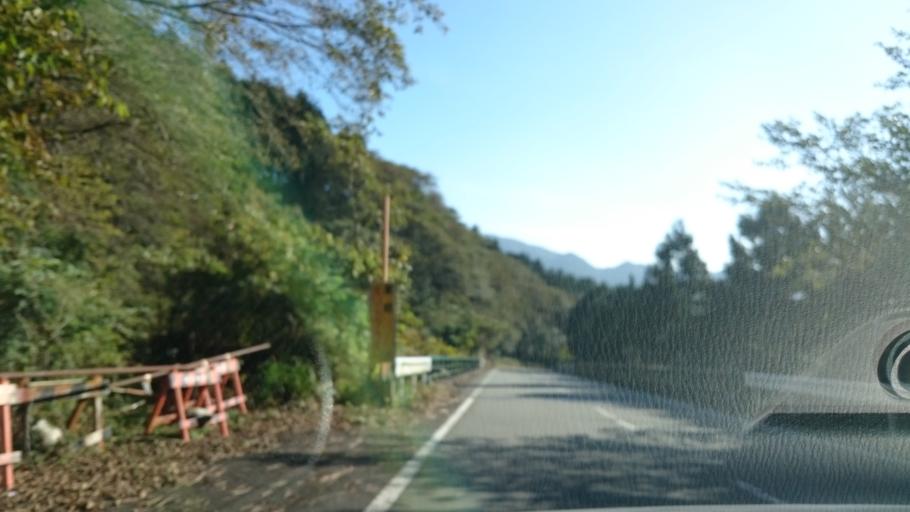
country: JP
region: Shizuoka
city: Heda
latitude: 34.9806
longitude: 138.8133
